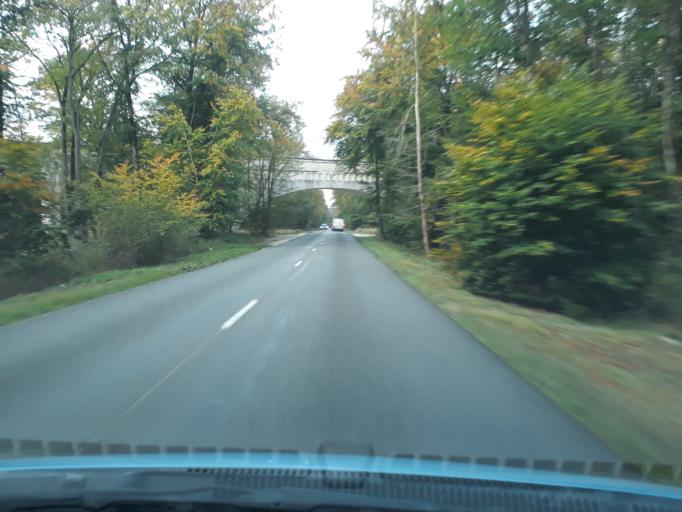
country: FR
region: Ile-de-France
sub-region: Departement de Seine-et-Marne
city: Avon
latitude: 48.3802
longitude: 2.7443
